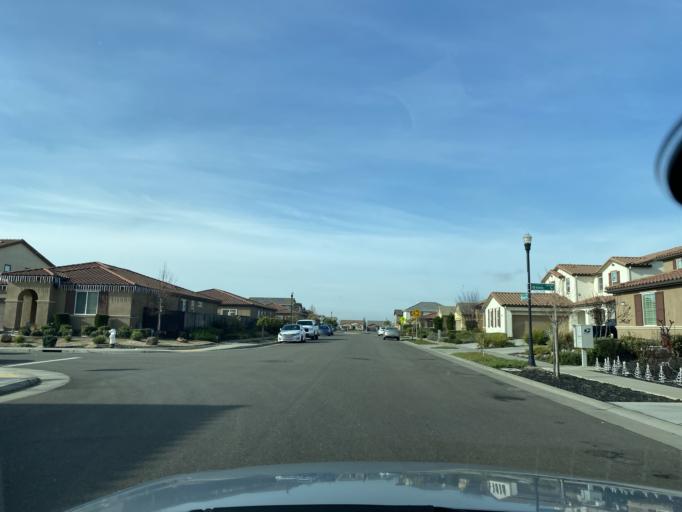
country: US
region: California
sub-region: Sacramento County
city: Elk Grove
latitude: 38.3925
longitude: -121.3930
